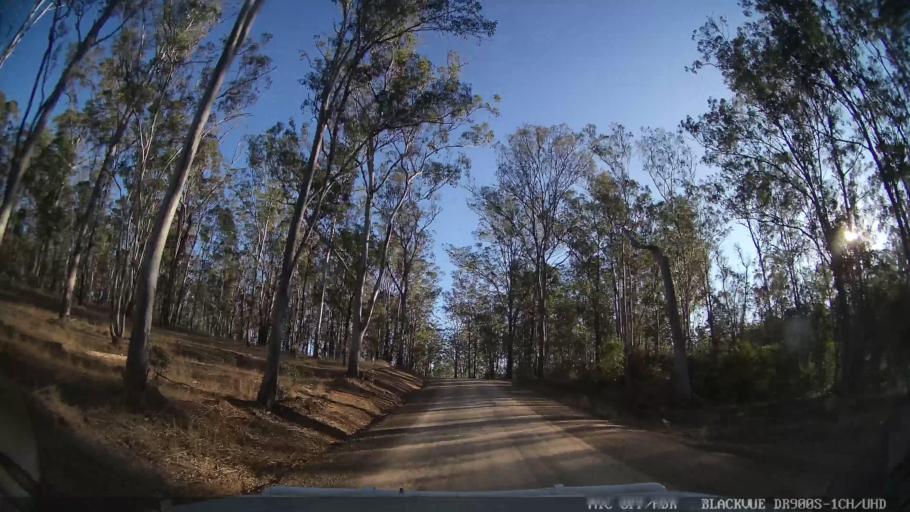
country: AU
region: Queensland
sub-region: Gladstone
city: Toolooa
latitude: -24.6819
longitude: 151.3331
